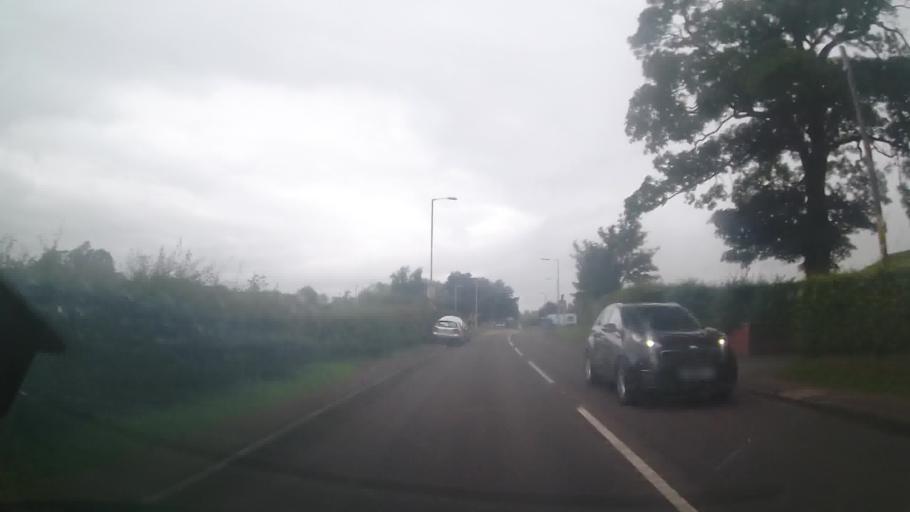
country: GB
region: England
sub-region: Shropshire
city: Whitchurch
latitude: 52.9567
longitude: -2.6736
